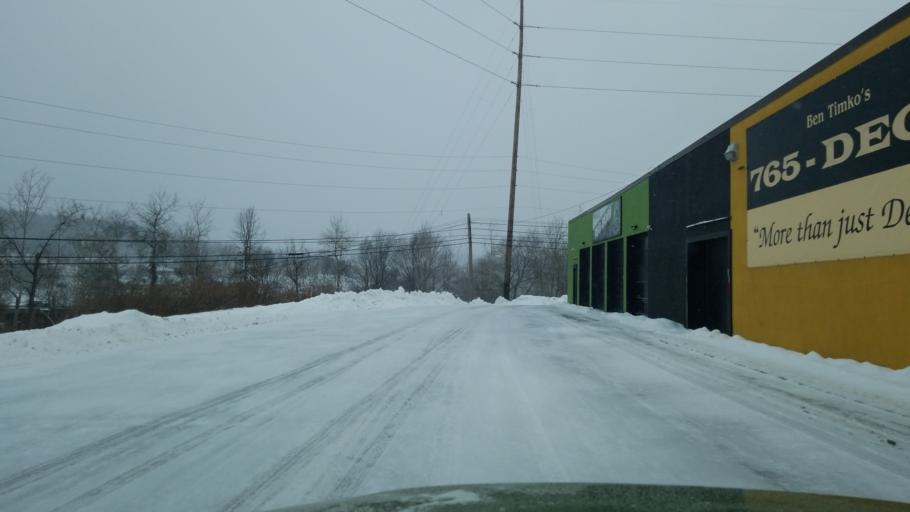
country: US
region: Pennsylvania
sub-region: Clearfield County
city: Clearfield
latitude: 41.0246
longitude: -78.4142
